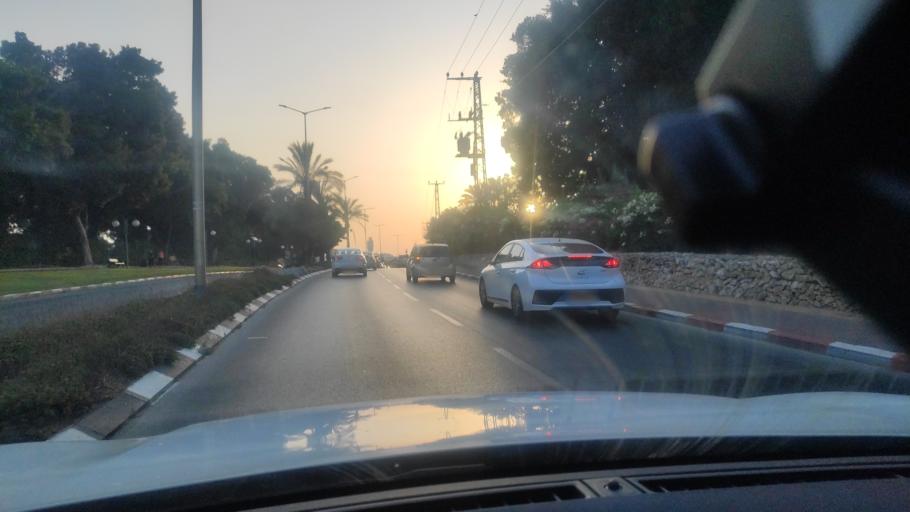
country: IL
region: Central District
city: Kfar Saba
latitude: 32.1831
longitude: 34.9220
